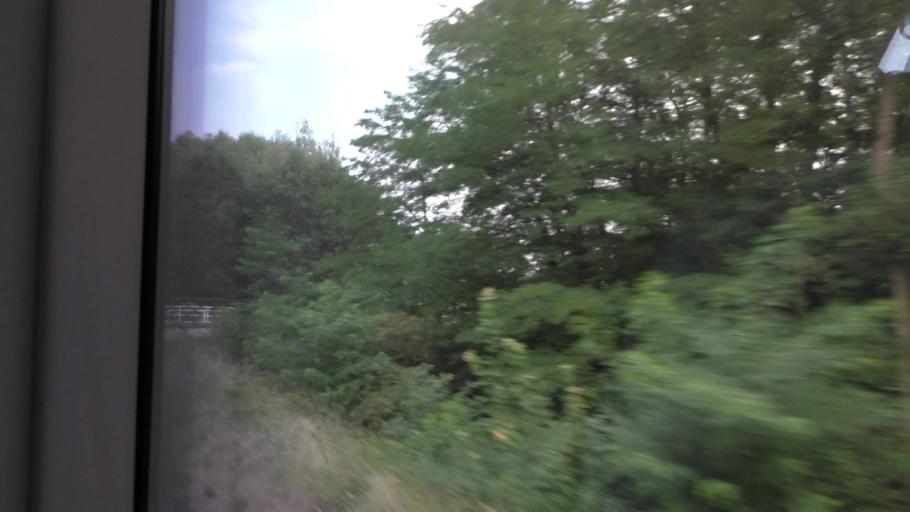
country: DE
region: Brandenburg
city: Mixdorf
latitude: 52.1962
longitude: 14.3937
